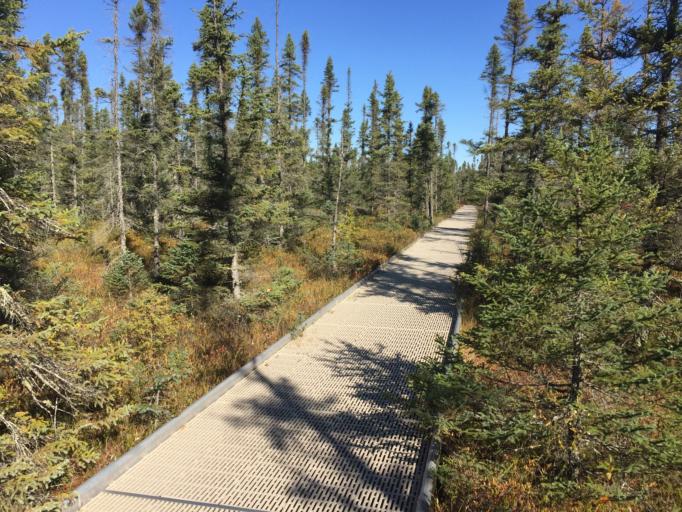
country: US
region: Minnesota
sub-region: Lake of the Woods County
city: Baudette
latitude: 48.2956
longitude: -94.5670
